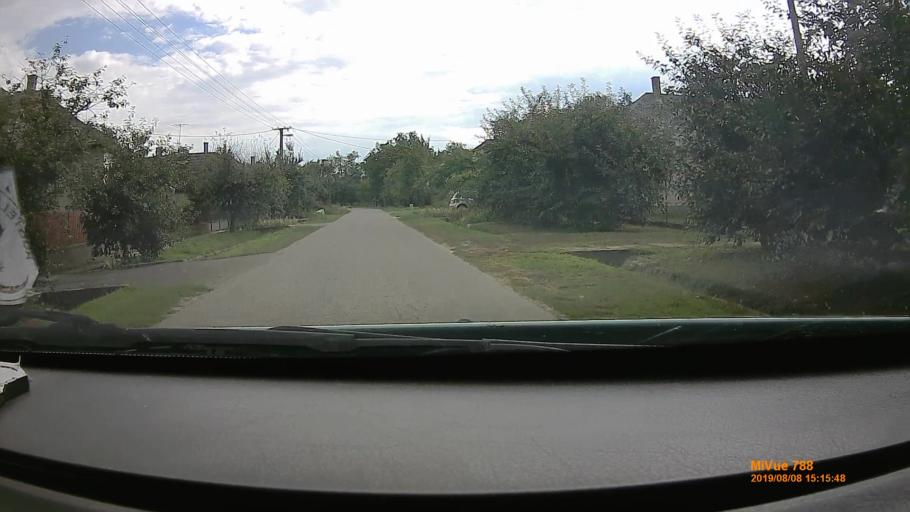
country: HU
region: Szabolcs-Szatmar-Bereg
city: Tunyogmatolcs
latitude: 47.9672
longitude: 22.4579
